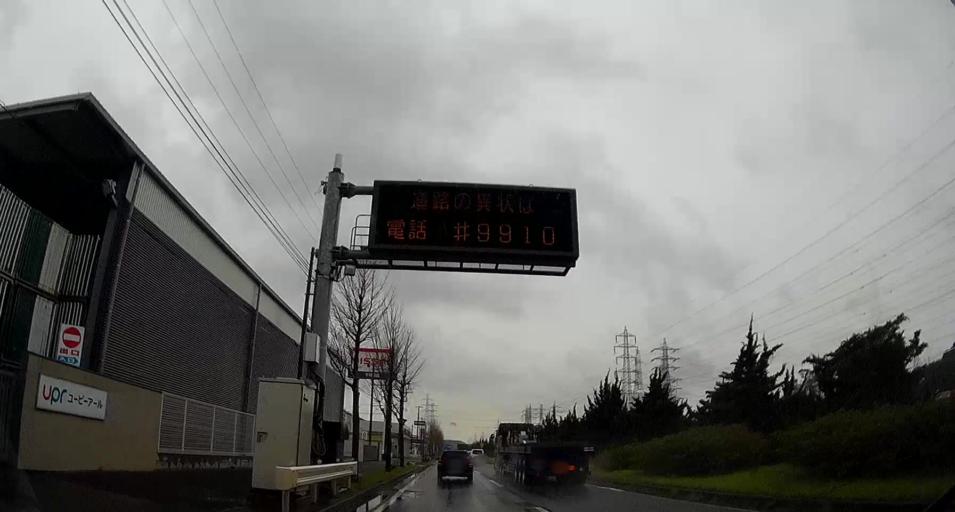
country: JP
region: Chiba
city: Ichihara
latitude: 35.4786
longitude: 140.0340
